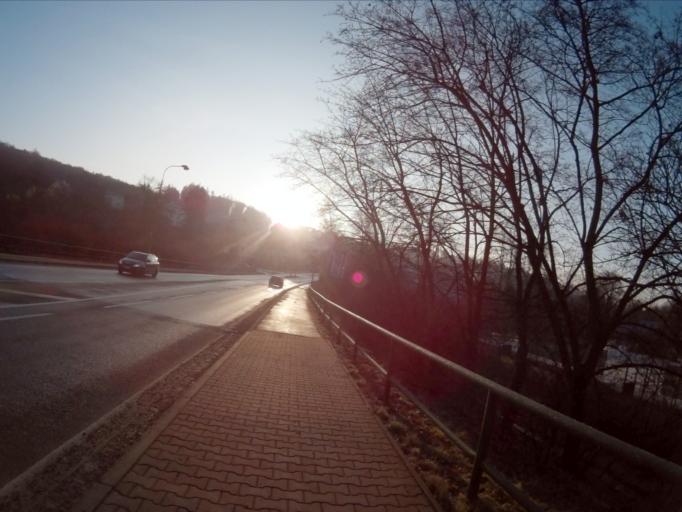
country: CZ
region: Vysocina
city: Namest' nad Oslavou
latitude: 49.2046
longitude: 16.1567
